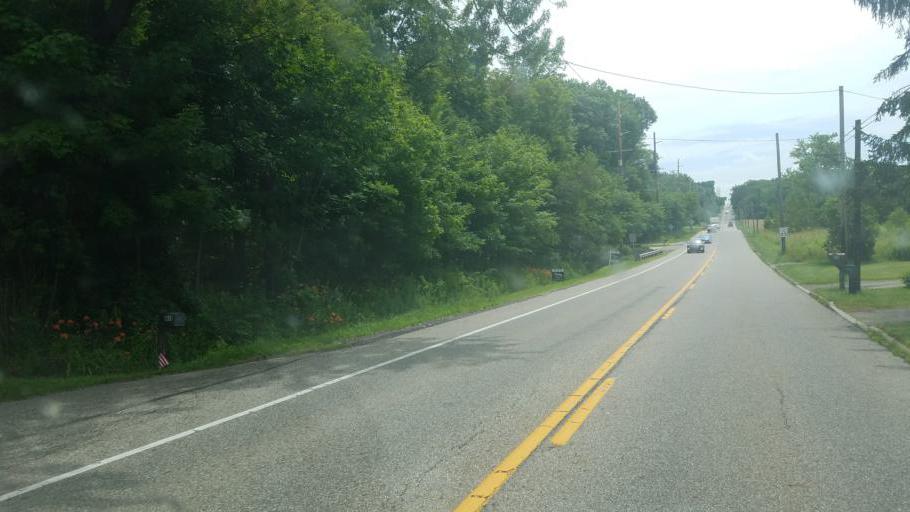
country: US
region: Ohio
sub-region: Geauga County
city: Bainbridge
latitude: 41.4104
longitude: -81.3350
